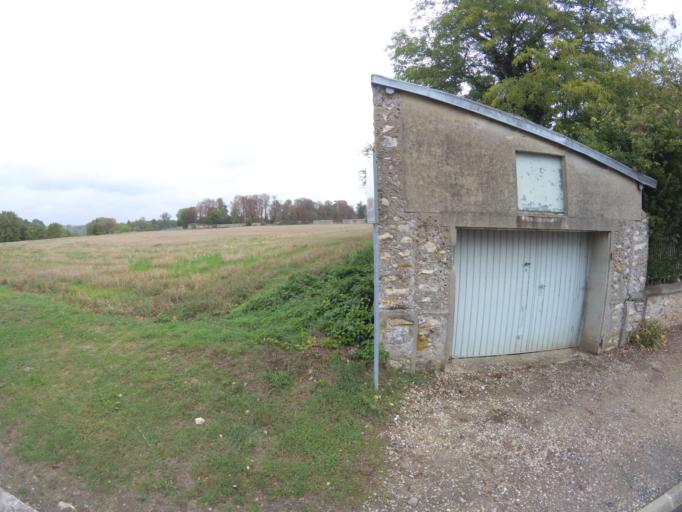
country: FR
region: Ile-de-France
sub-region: Departement de Seine-et-Marne
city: Gouvernes
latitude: 48.8499
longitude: 2.6911
